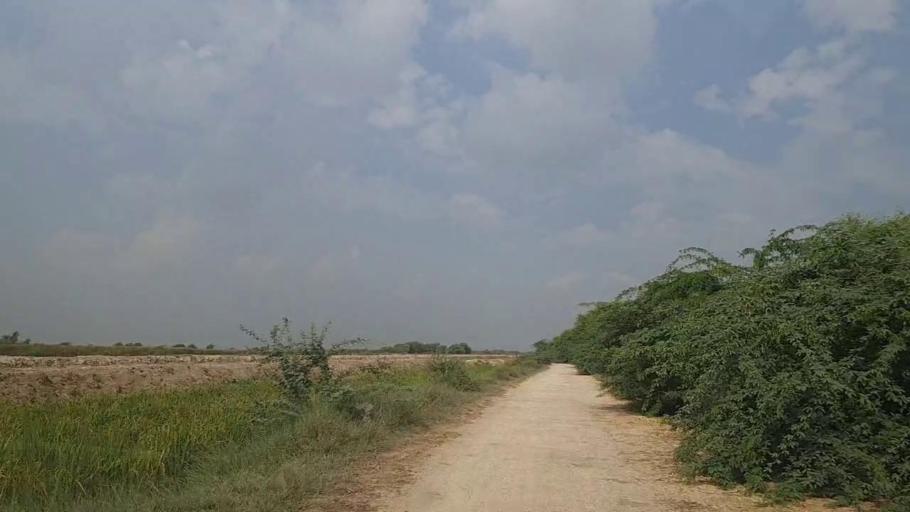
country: PK
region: Sindh
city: Daro Mehar
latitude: 24.6934
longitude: 68.1264
